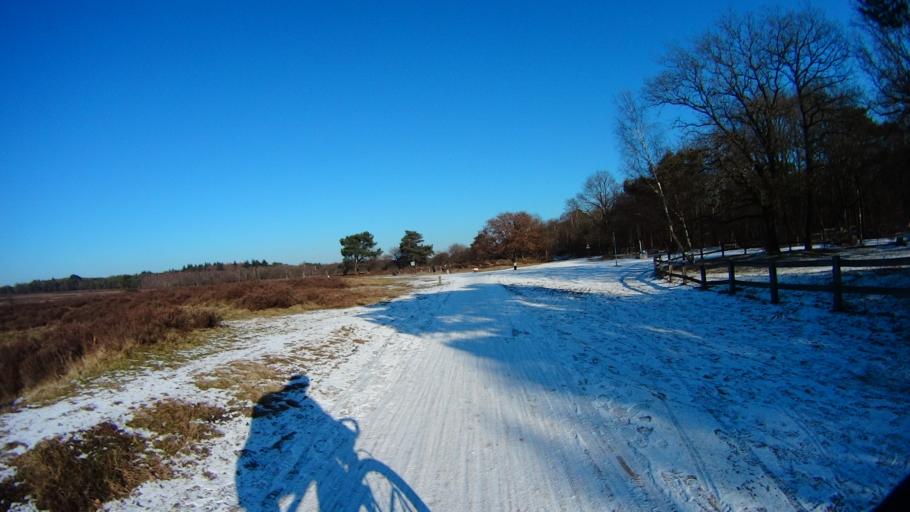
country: NL
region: North Holland
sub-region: Gemeente Laren
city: Laren
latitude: 52.2355
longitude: 5.2206
